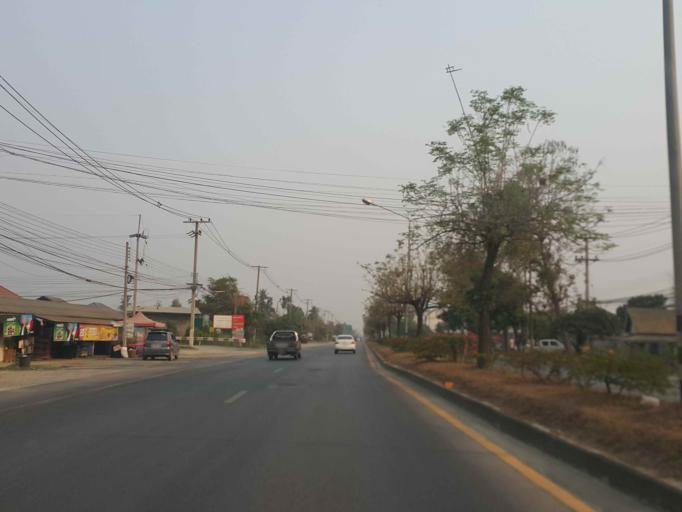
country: TH
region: Chiang Mai
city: San Sai
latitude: 18.9261
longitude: 98.9921
